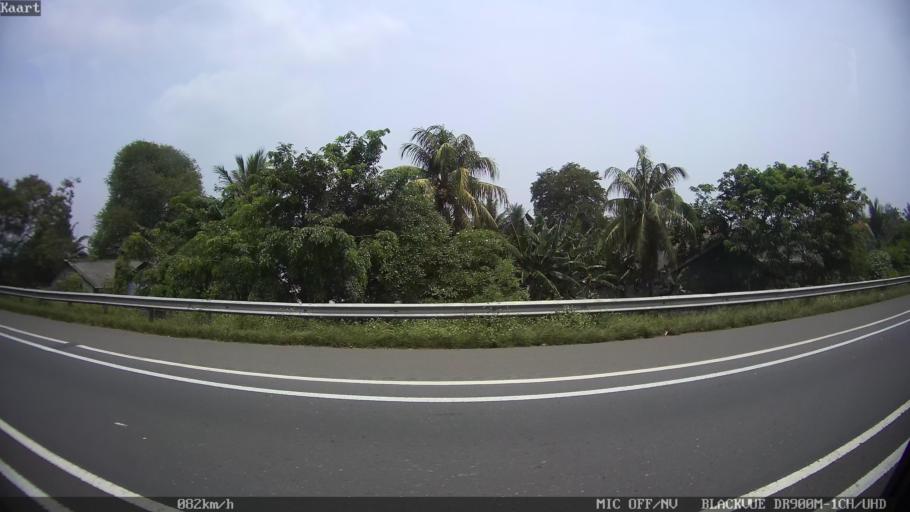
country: ID
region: West Java
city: Kresek
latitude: -6.1524
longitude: 106.3167
